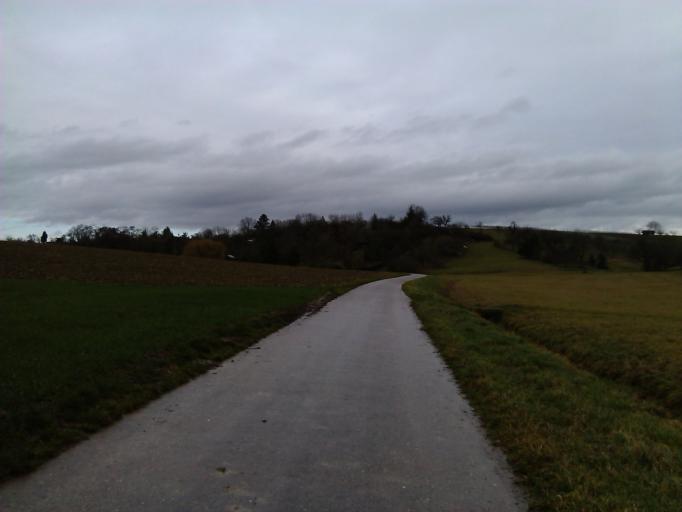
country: DE
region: Baden-Wuerttemberg
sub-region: Regierungsbezirk Stuttgart
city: Bad Wimpfen
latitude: 49.2112
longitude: 9.1601
